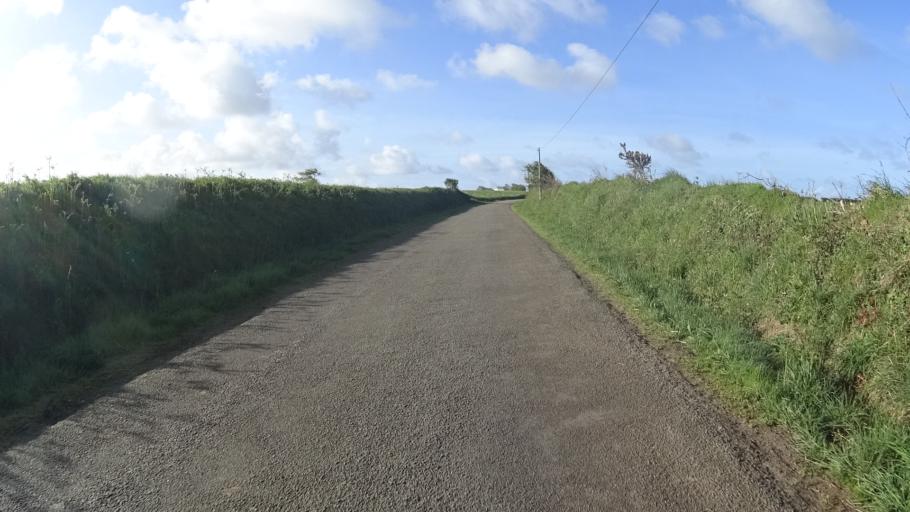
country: FR
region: Brittany
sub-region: Departement du Finistere
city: Ploumoguer
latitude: 48.4205
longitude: -4.6889
